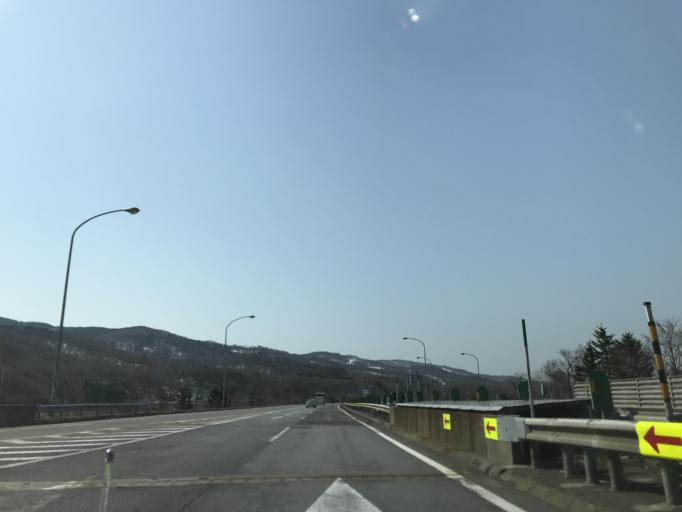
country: JP
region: Hokkaido
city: Bibai
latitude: 43.3319
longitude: 141.8882
